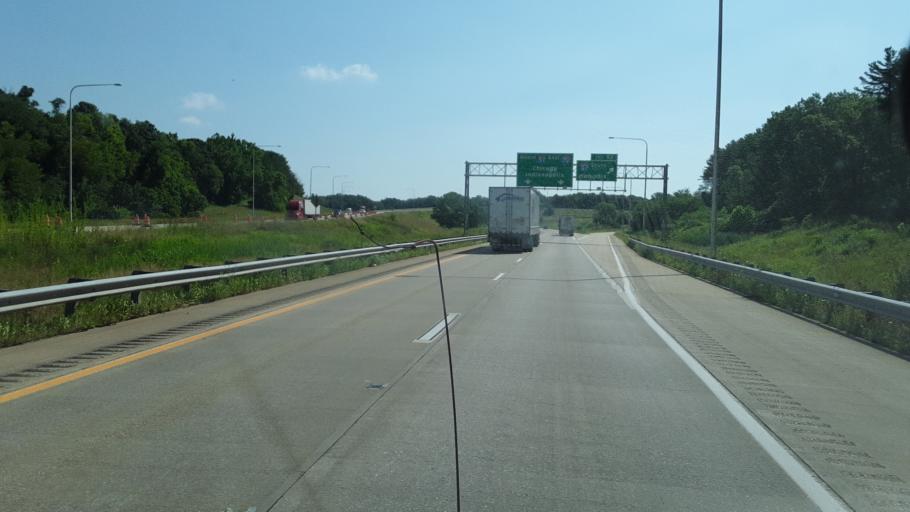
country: US
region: Illinois
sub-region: Effingham County
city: Effingham
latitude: 39.0923
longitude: -88.5876
